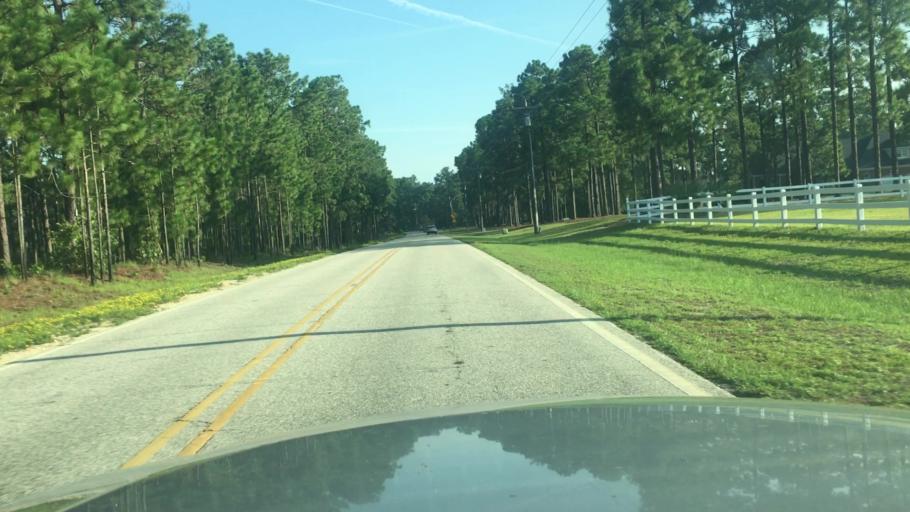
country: US
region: North Carolina
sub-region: Harnett County
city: Walkertown
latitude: 35.2205
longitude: -78.8658
